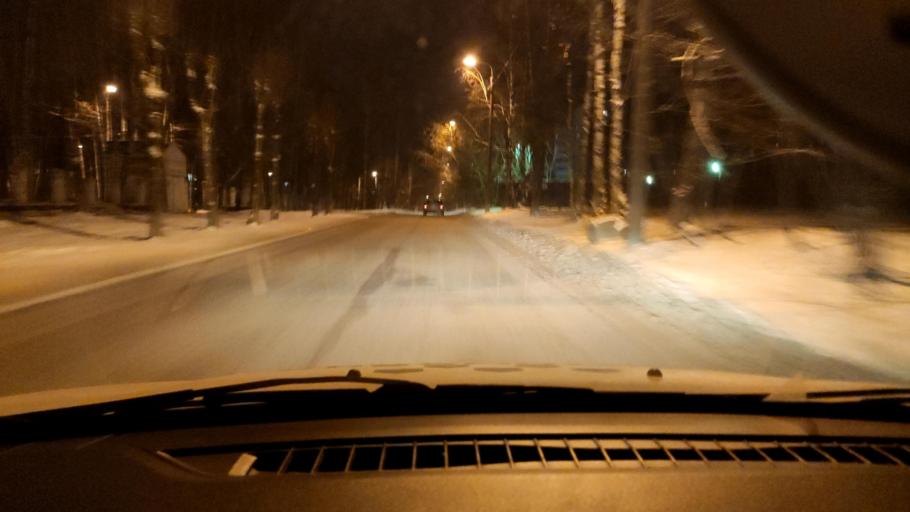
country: RU
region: Perm
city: Kultayevo
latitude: 58.0100
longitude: 55.9621
